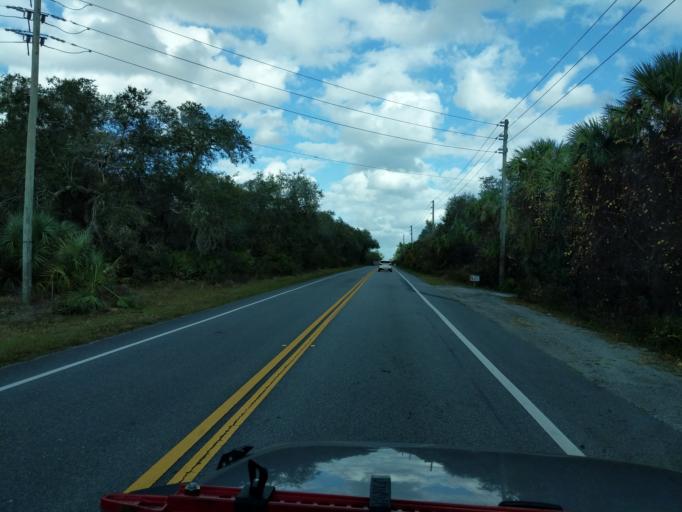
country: US
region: Florida
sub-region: Seminole County
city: Geneva
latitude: 28.7030
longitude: -81.1317
